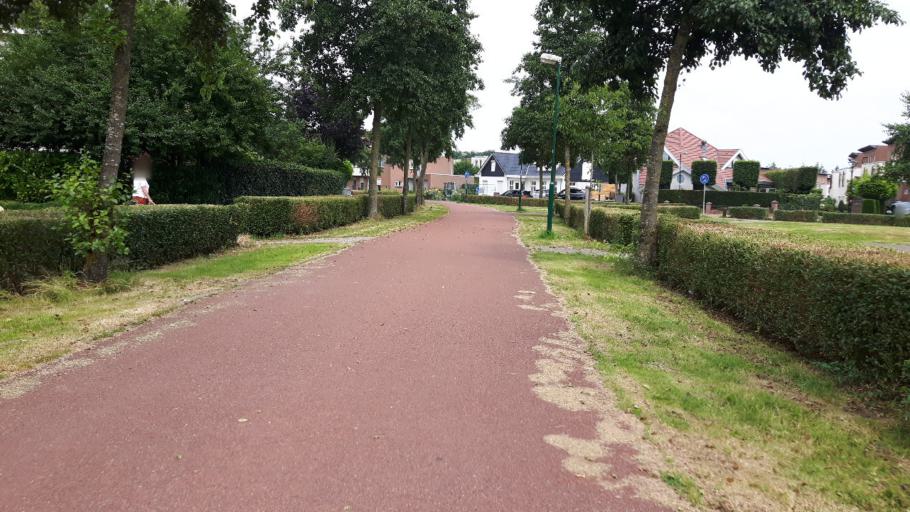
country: NL
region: Utrecht
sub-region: Gemeente Houten
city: Houten
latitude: 52.0234
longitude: 5.1845
